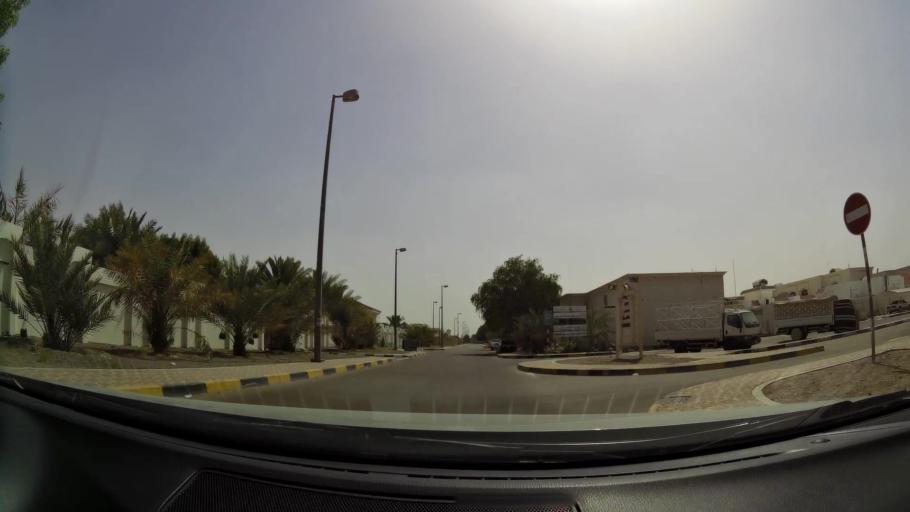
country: AE
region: Abu Dhabi
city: Al Ain
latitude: 24.2230
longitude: 55.6857
